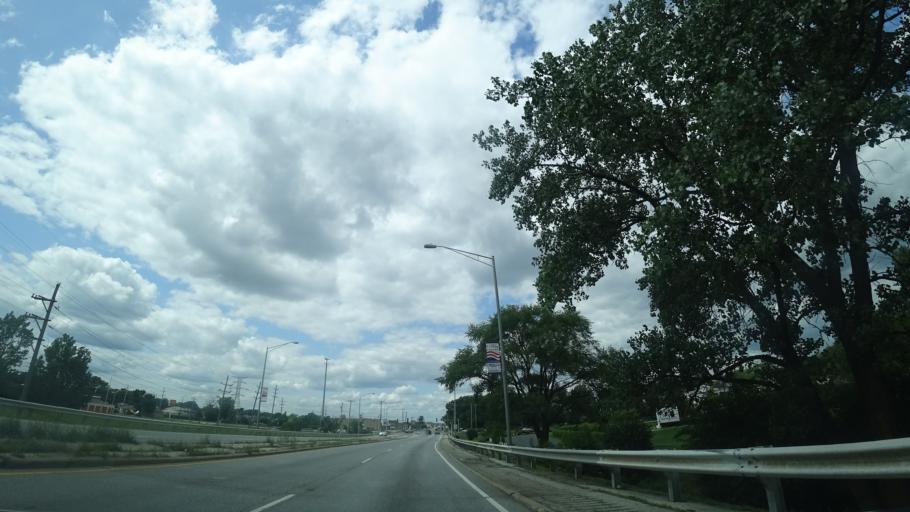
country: US
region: Illinois
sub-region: Cook County
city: Alsip
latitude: 41.6817
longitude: -87.7392
